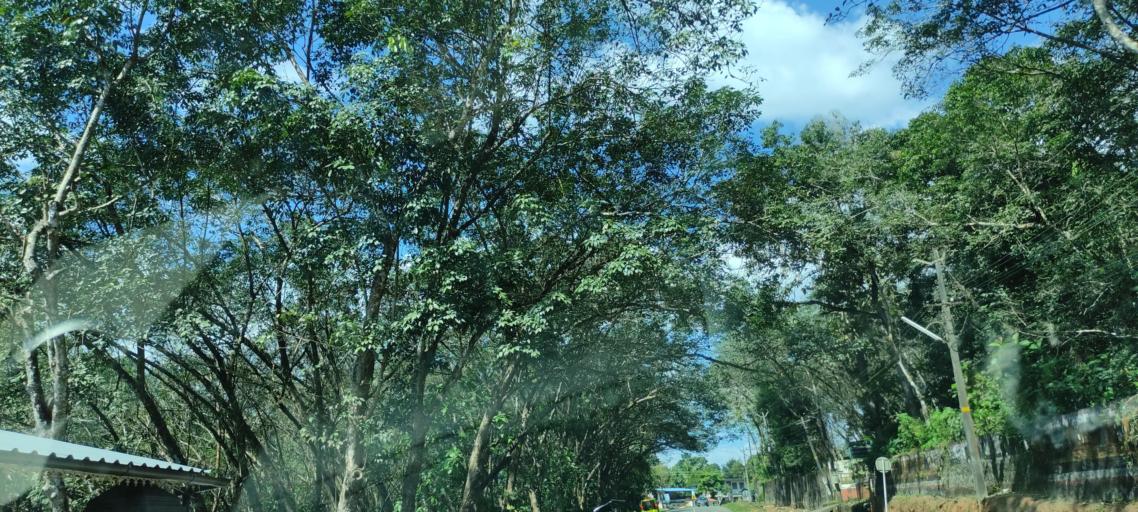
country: IN
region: Kerala
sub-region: Pattanamtitta
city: Adur
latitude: 9.1085
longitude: 76.6947
